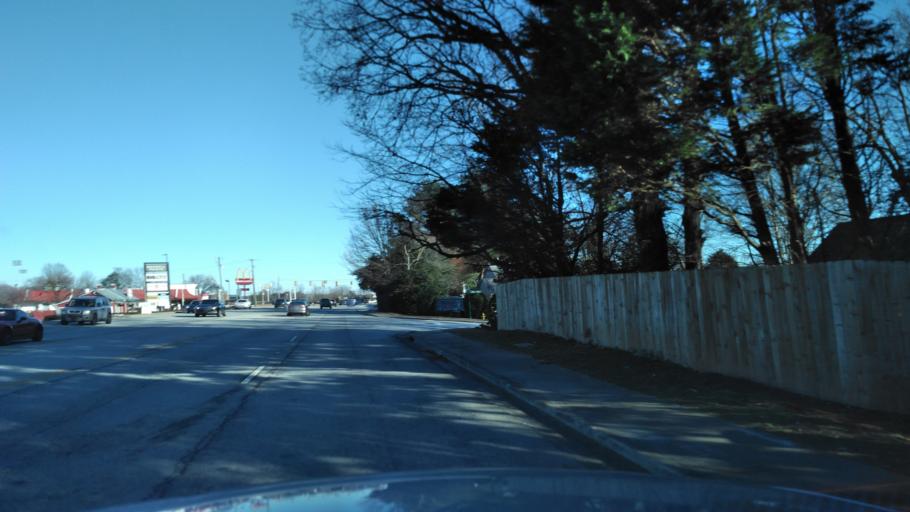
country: US
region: South Carolina
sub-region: Greenville County
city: Five Forks
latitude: 34.8201
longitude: -82.2587
